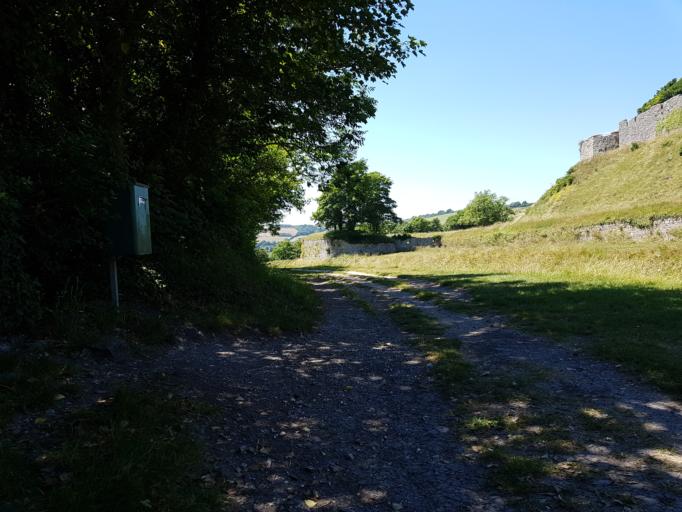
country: GB
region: England
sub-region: Isle of Wight
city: Newport
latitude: 50.6866
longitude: -1.3120
